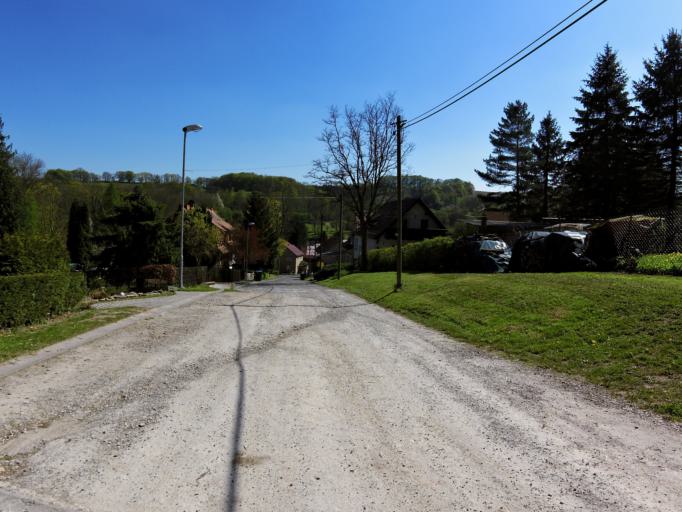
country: DE
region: Thuringia
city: Wolfsburg-Unkeroda
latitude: 50.9389
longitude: 10.2508
